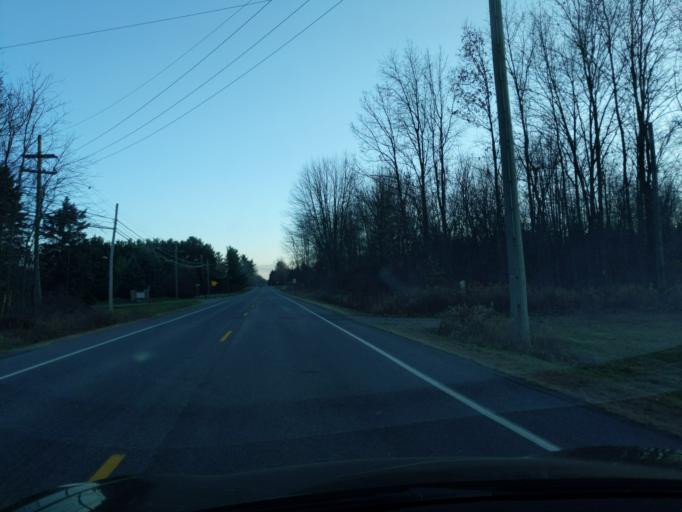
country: US
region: Michigan
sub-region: Ingham County
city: Williamston
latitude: 42.7013
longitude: -84.3137
